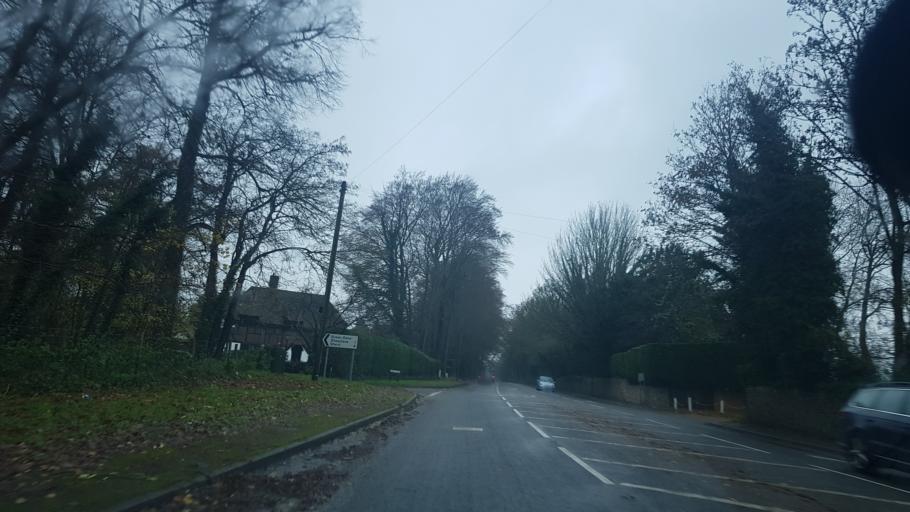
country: GB
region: England
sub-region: Surrey
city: East Horsley
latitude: 51.2612
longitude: -0.4235
